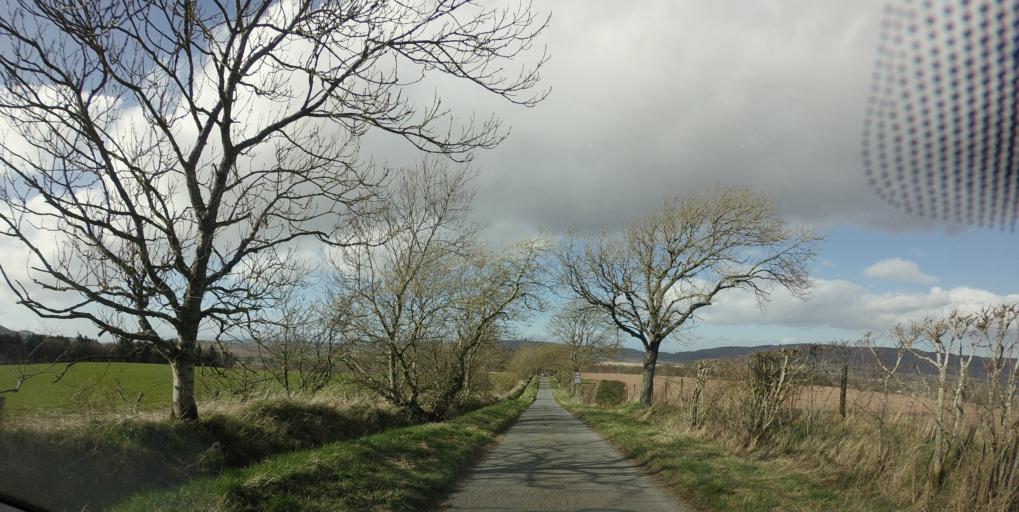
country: GB
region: Scotland
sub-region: Perth and Kinross
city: Bridge of Earn
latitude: 56.3277
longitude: -3.4151
